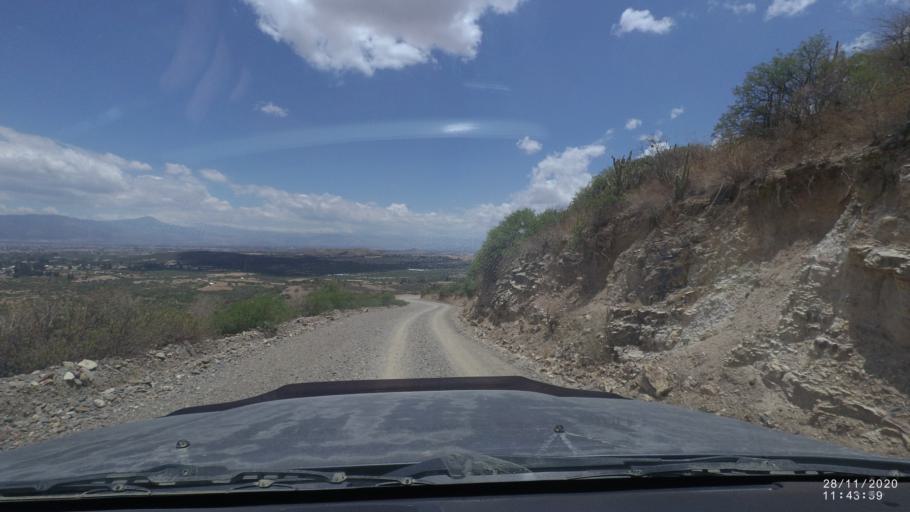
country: BO
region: Cochabamba
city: Tarata
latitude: -17.6610
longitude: -66.0449
